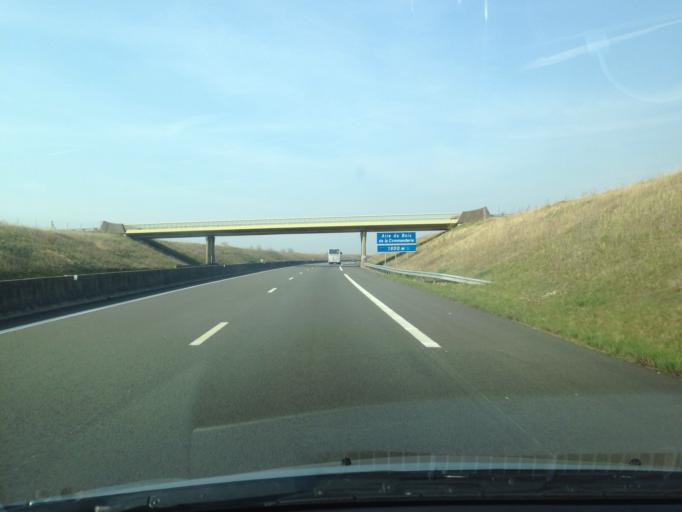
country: FR
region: Nord-Pas-de-Calais
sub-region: Departement du Pas-de-Calais
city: Verton
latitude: 50.3575
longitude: 1.6887
